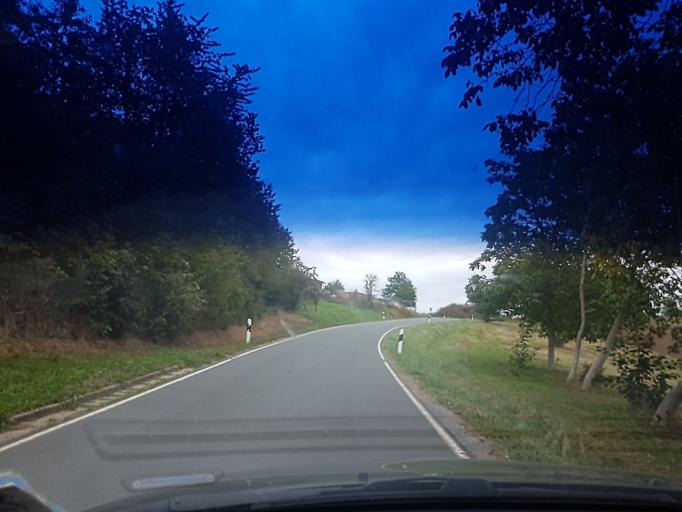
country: DE
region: Bavaria
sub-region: Regierungsbezirk Unterfranken
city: Geiselwind
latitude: 49.8008
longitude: 10.4921
